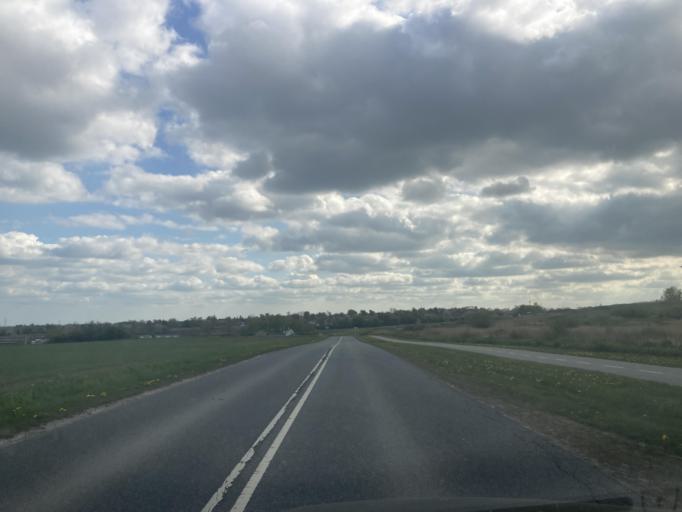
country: DK
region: Zealand
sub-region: Greve Kommune
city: Tune
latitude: 55.6042
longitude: 12.1796
